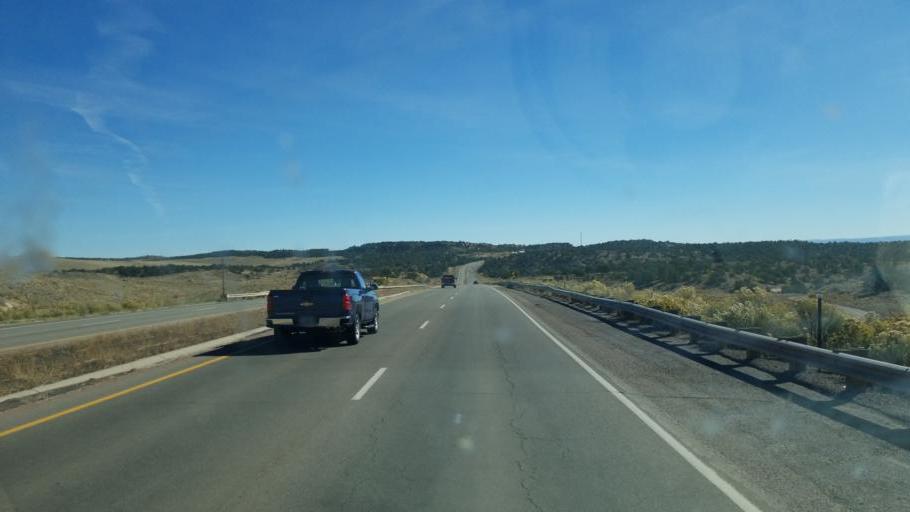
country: US
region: Arizona
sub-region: Apache County
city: Window Rock
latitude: 35.6373
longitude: -108.9861
